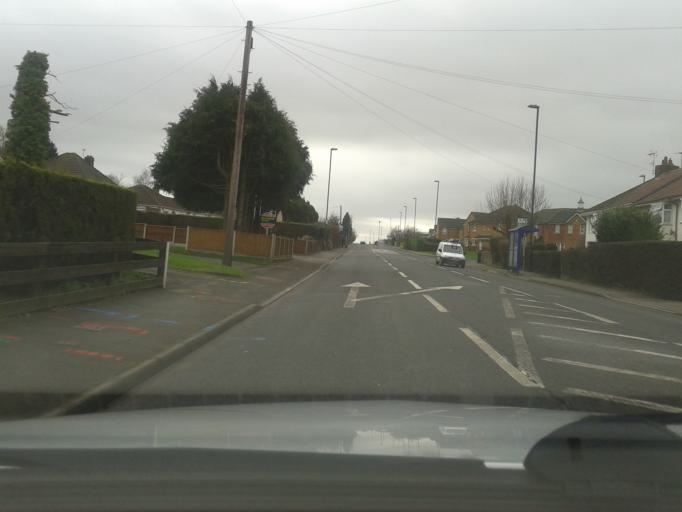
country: GB
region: England
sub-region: South Gloucestershire
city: Winterbourne
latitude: 51.5313
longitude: -2.4624
